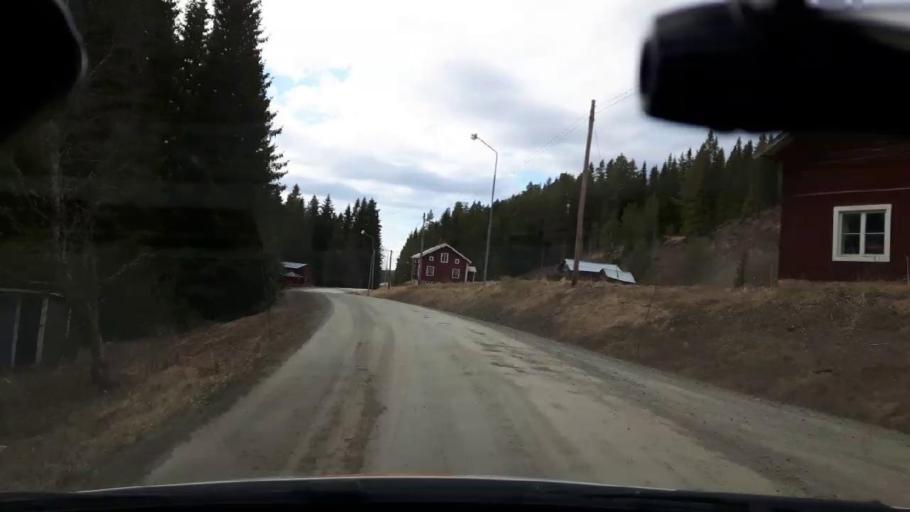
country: SE
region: Jaemtland
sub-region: OEstersunds Kommun
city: Brunflo
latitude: 62.9458
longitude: 14.6664
